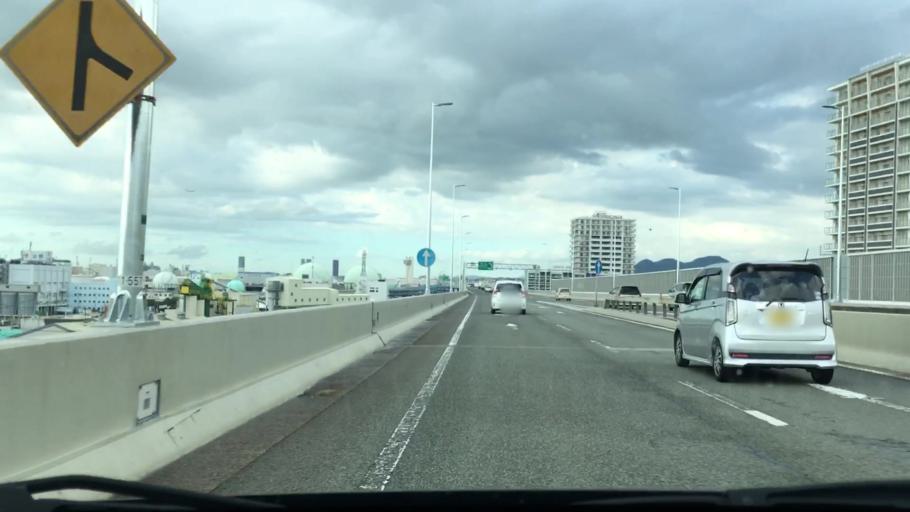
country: JP
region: Fukuoka
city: Fukuoka-shi
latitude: 33.6095
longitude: 130.4085
